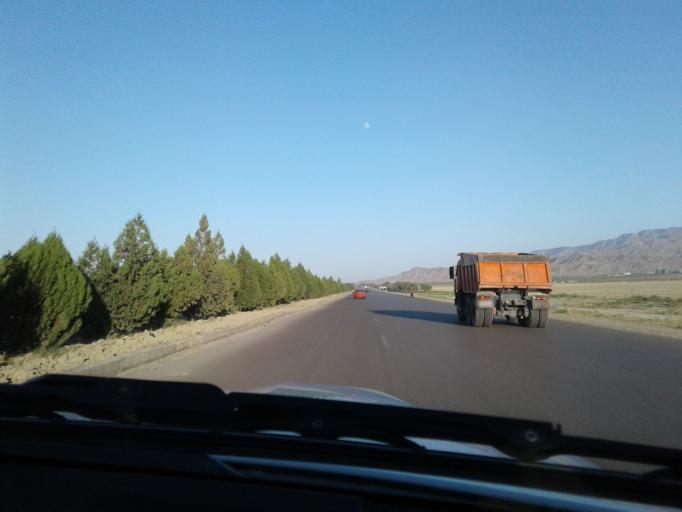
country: TM
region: Ahal
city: Baharly
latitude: 38.3004
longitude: 57.6316
